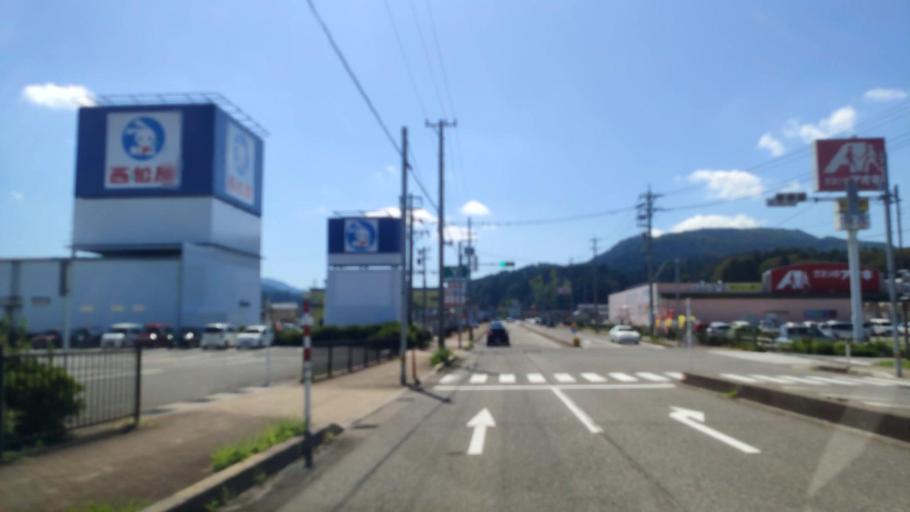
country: JP
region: Ishikawa
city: Nanao
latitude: 37.3875
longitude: 136.9025
